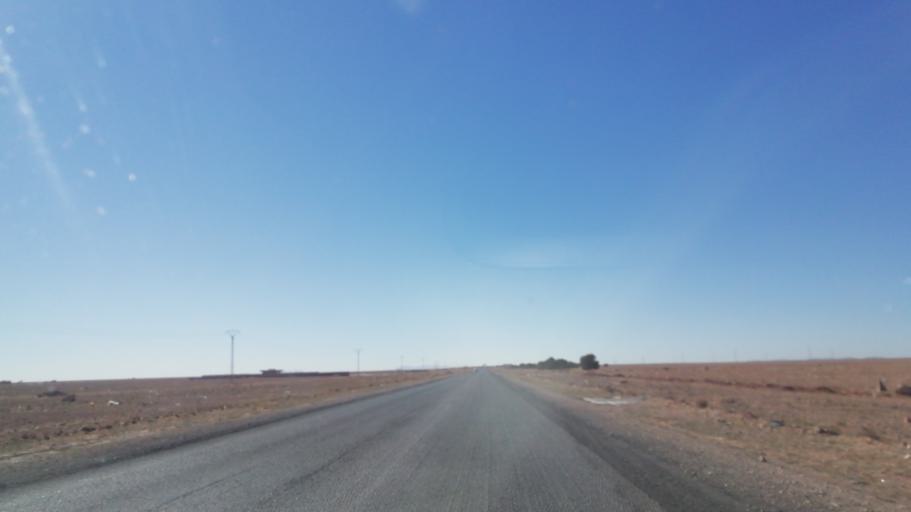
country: DZ
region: Saida
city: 'Ain el Hadjar
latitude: 34.0184
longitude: 0.0616
